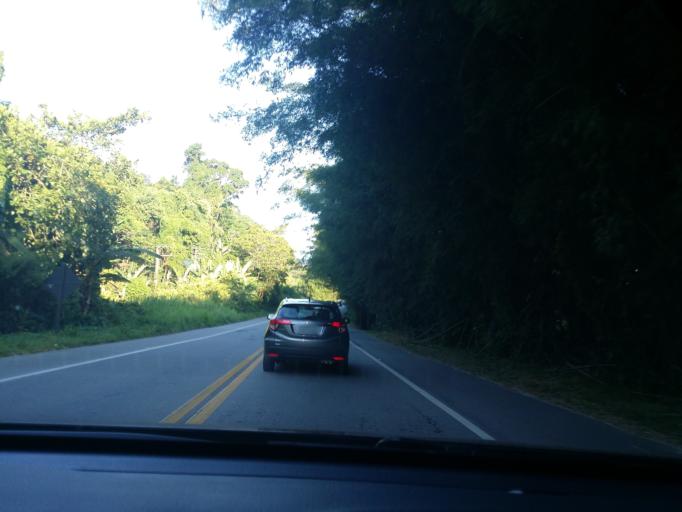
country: BR
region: Sao Paulo
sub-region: Sao Sebastiao
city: Sao Sebastiao
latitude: -23.7702
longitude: -45.7097
